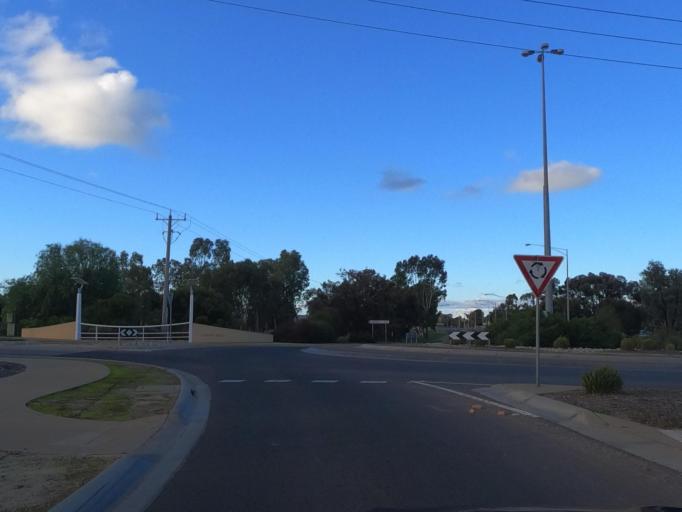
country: AU
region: Victoria
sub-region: Swan Hill
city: Swan Hill
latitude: -35.3431
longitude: 143.5312
